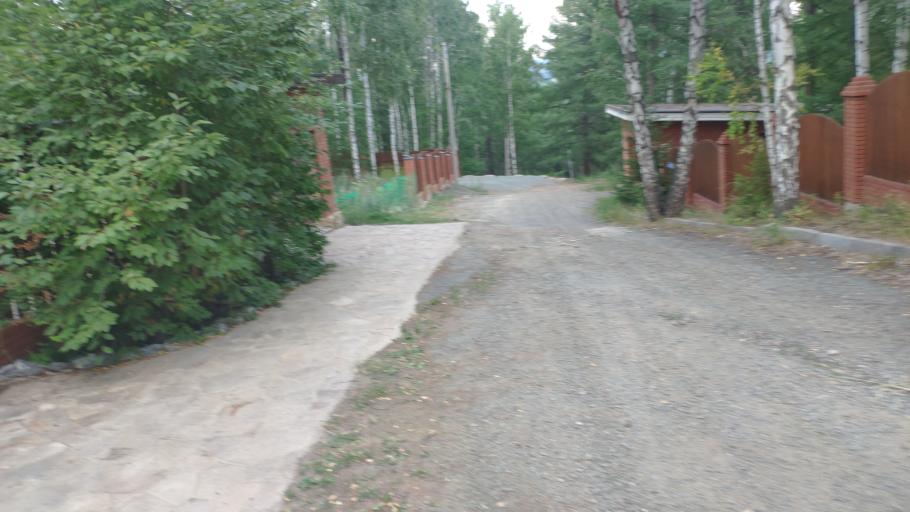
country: RU
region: Bashkortostan
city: Abzakovo
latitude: 53.8037
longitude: 58.6443
